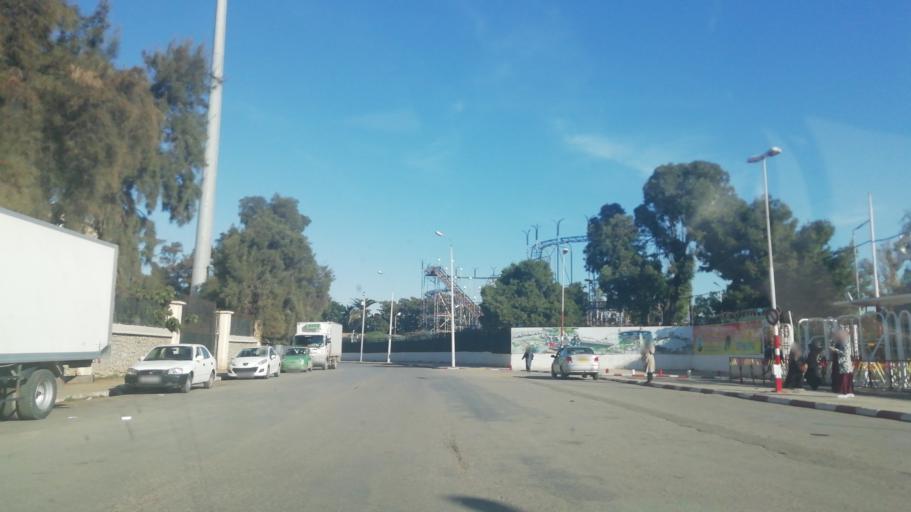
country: DZ
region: Oran
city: Oran
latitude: 35.6834
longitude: -0.6351
